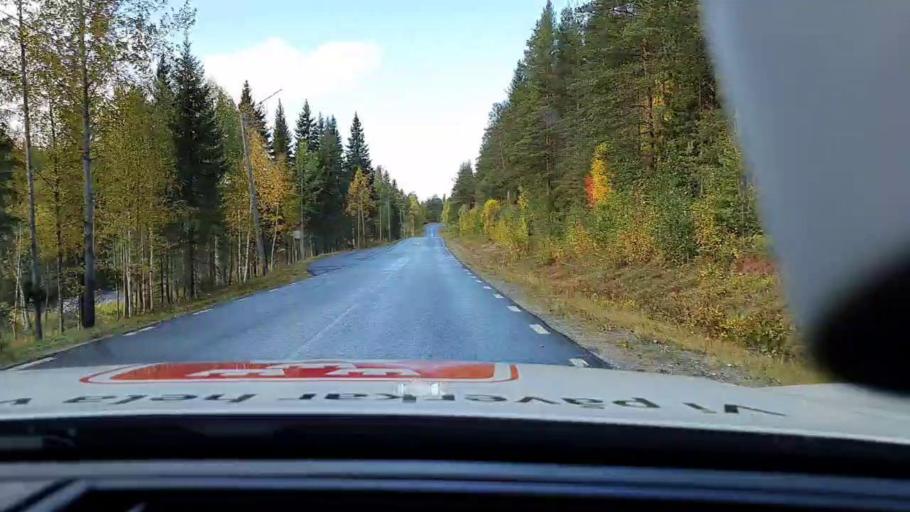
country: SE
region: Vaesterbotten
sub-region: Skelleftea Kommun
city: Langsele
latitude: 64.9449
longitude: 20.0316
